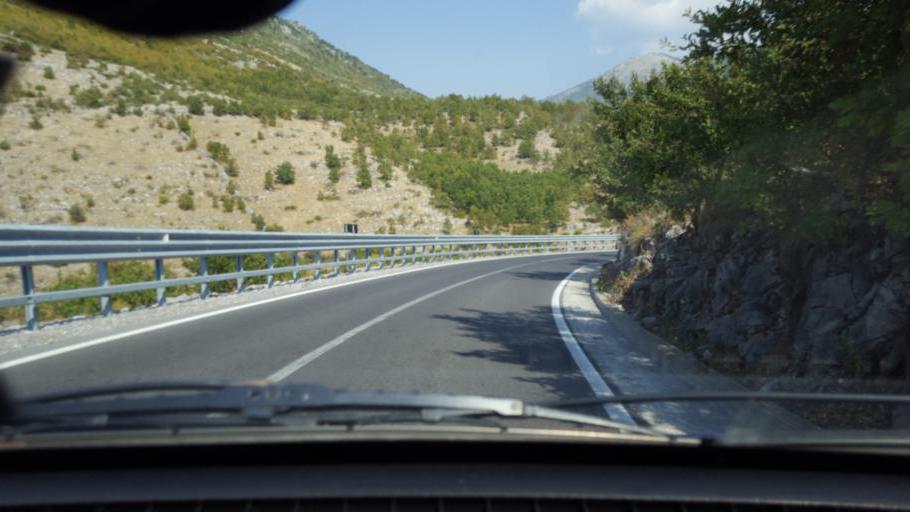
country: AL
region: Shkoder
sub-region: Rrethi i Malesia e Madhe
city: Hot
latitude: 42.3731
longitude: 19.4678
